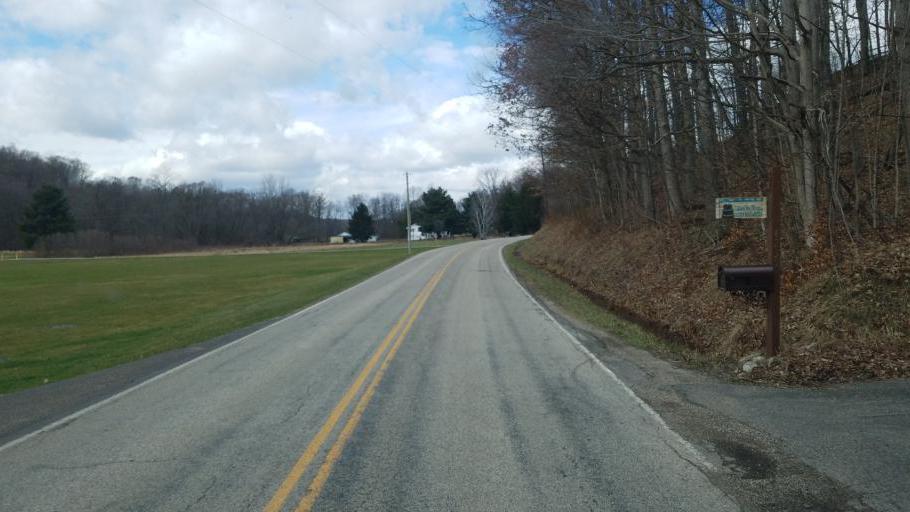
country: US
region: Ohio
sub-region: Sandusky County
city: Bellville
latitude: 40.6425
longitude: -82.4691
